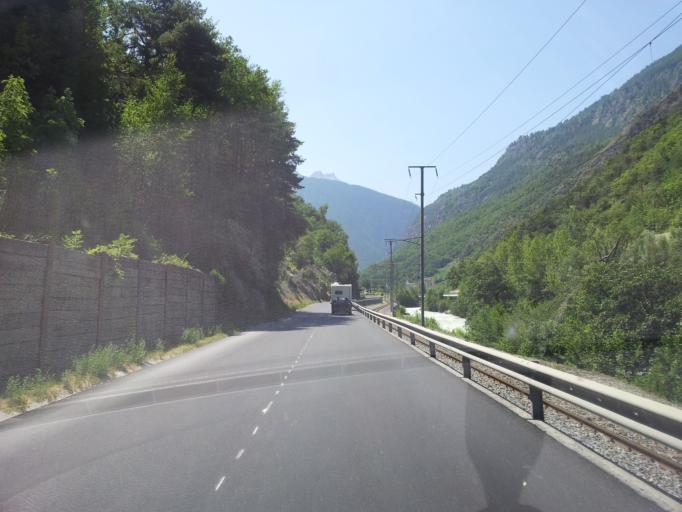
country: CH
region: Valais
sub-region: Visp District
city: Visp
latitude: 46.2708
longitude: 7.8816
